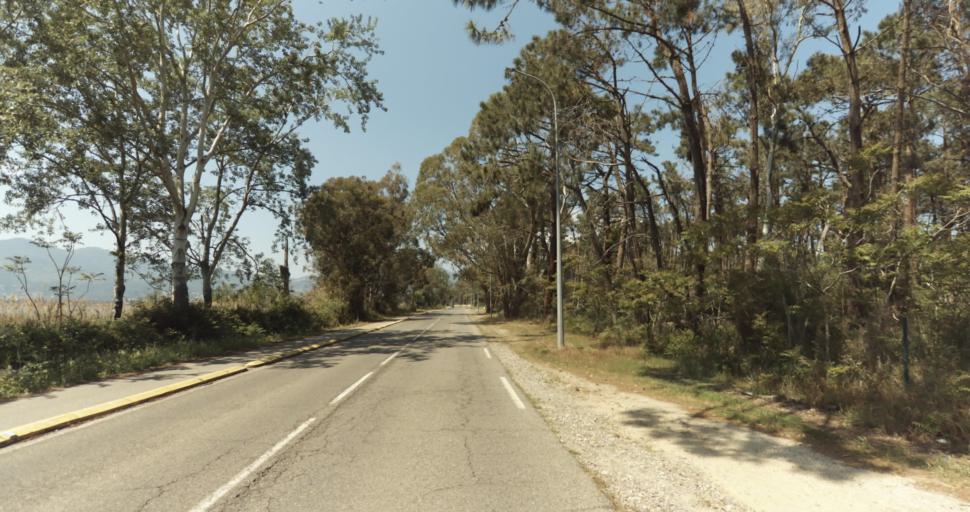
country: FR
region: Corsica
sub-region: Departement de la Haute-Corse
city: Biguglia
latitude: 42.6173
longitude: 9.4771
